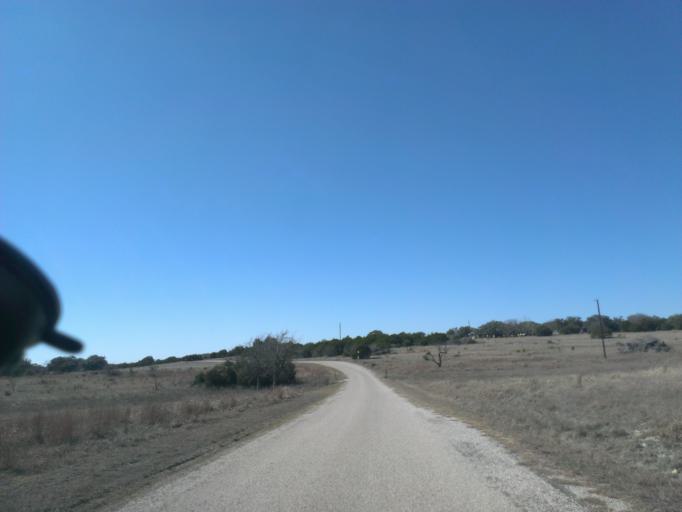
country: US
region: Texas
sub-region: Lampasas County
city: Kempner
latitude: 30.9201
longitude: -98.0591
